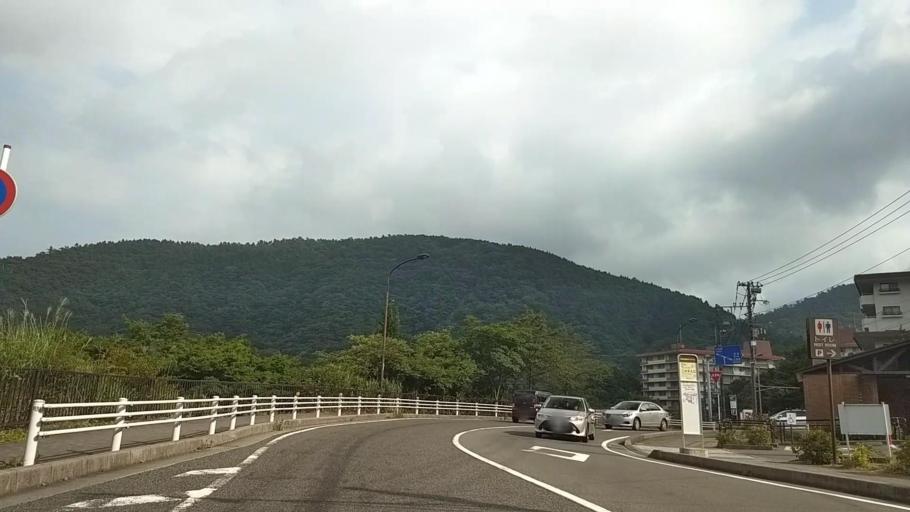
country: JP
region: Kanagawa
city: Hakone
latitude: 35.2412
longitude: 139.0494
